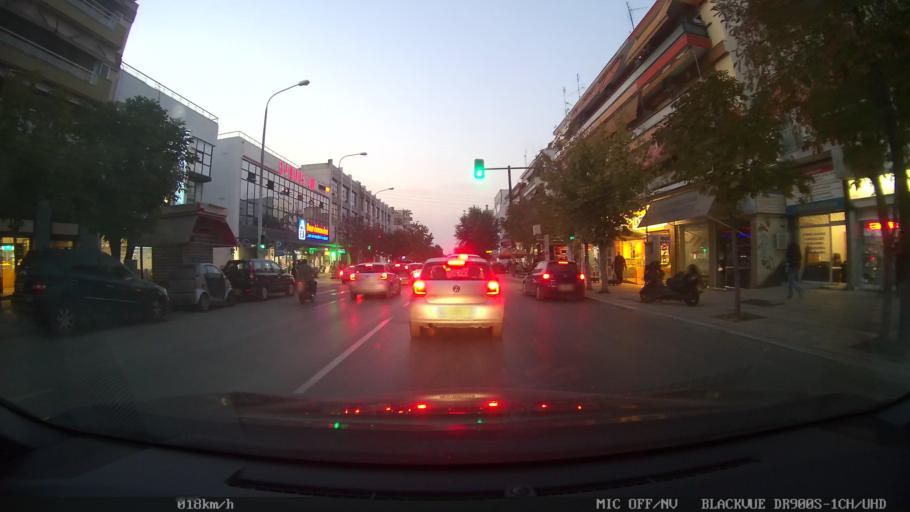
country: GR
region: Central Macedonia
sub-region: Nomos Thessalonikis
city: Kalamaria
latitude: 40.5874
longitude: 22.9619
